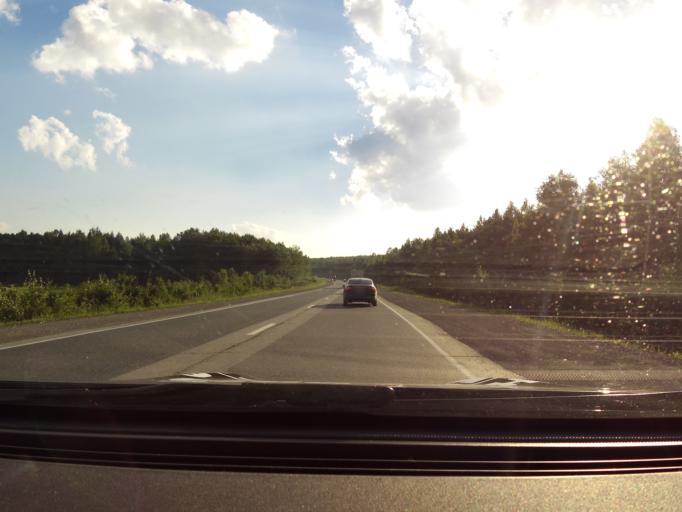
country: RU
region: Sverdlovsk
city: Talitsa
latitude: 56.8449
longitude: 60.0204
